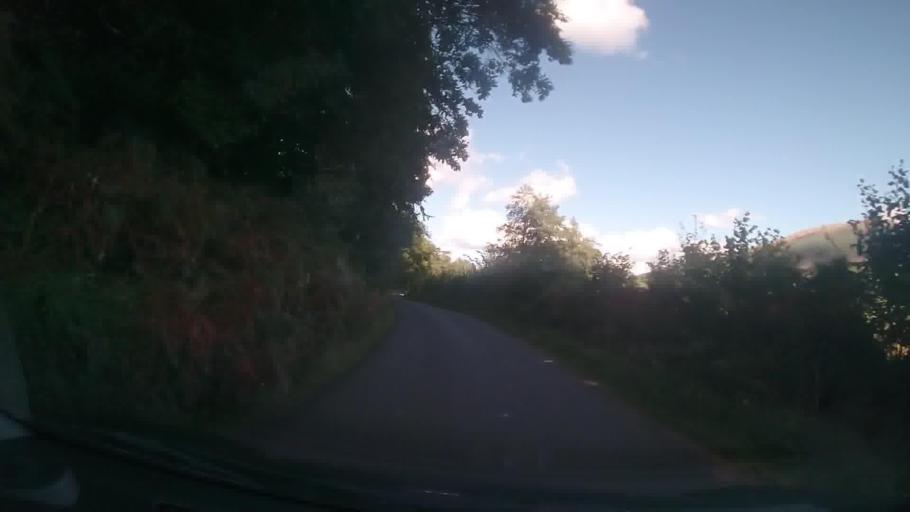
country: GB
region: Wales
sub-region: Caerphilly County Borough
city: Rhymney
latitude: 51.8598
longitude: -3.3138
